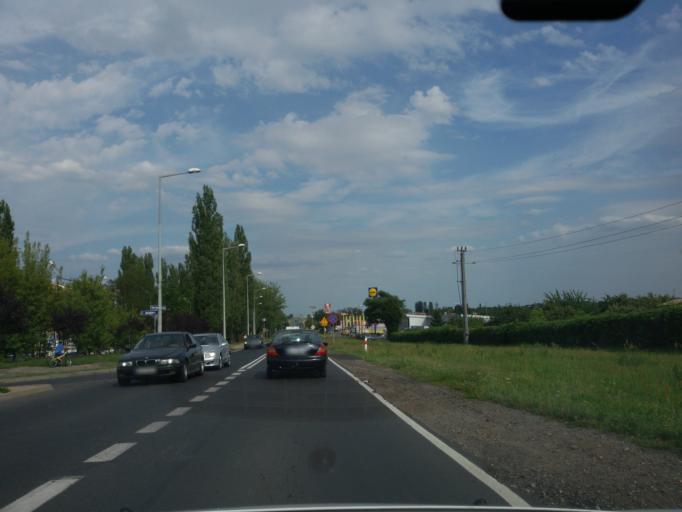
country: PL
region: Lower Silesian Voivodeship
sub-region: Powiat glogowski
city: Glogow
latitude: 51.6490
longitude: 16.0721
